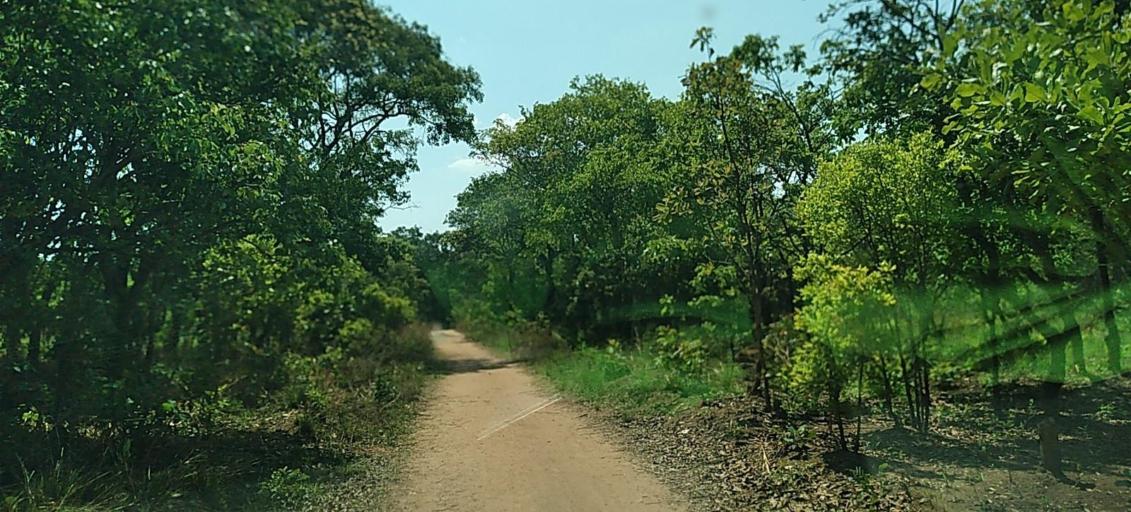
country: CD
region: Katanga
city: Kolwezi
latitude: -11.2765
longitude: 25.1173
